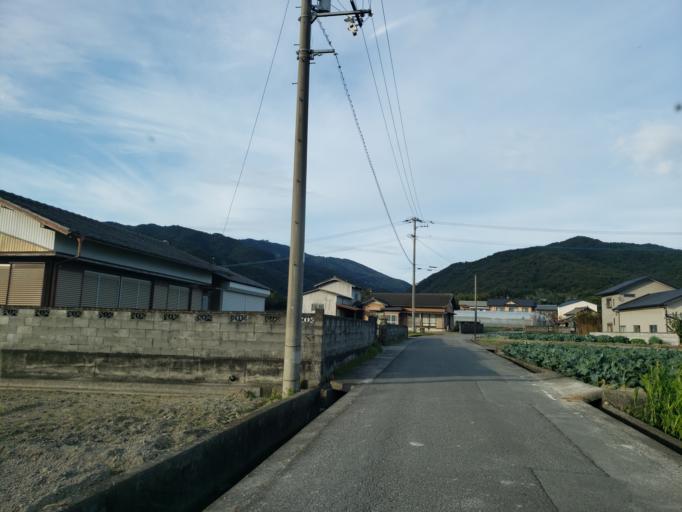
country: JP
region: Tokushima
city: Wakimachi
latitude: 34.0950
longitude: 134.2255
